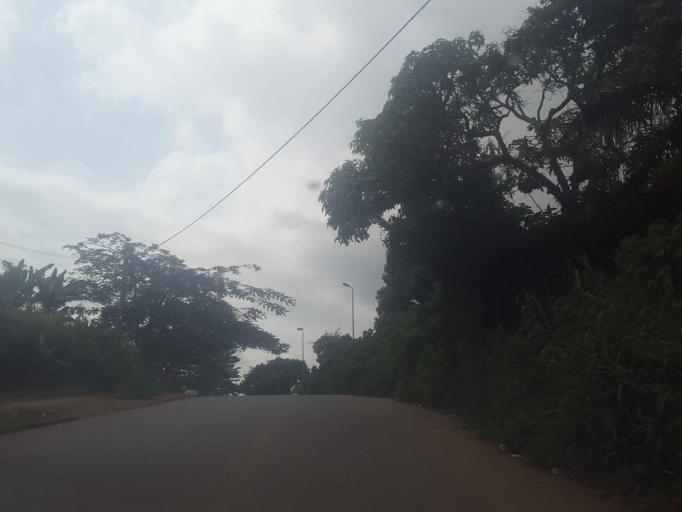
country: CM
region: Centre
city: Yaounde
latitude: 3.8721
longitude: 11.4844
